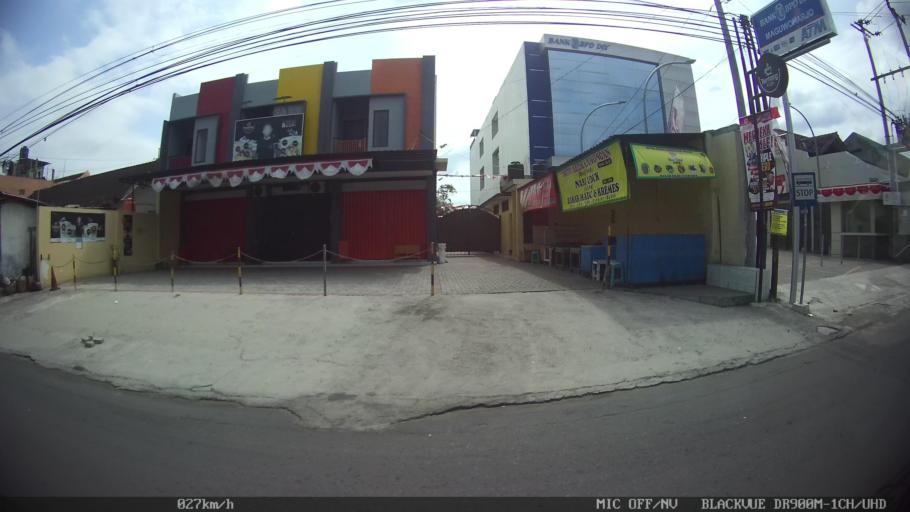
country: ID
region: Daerah Istimewa Yogyakarta
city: Depok
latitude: -7.7560
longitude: 110.4337
